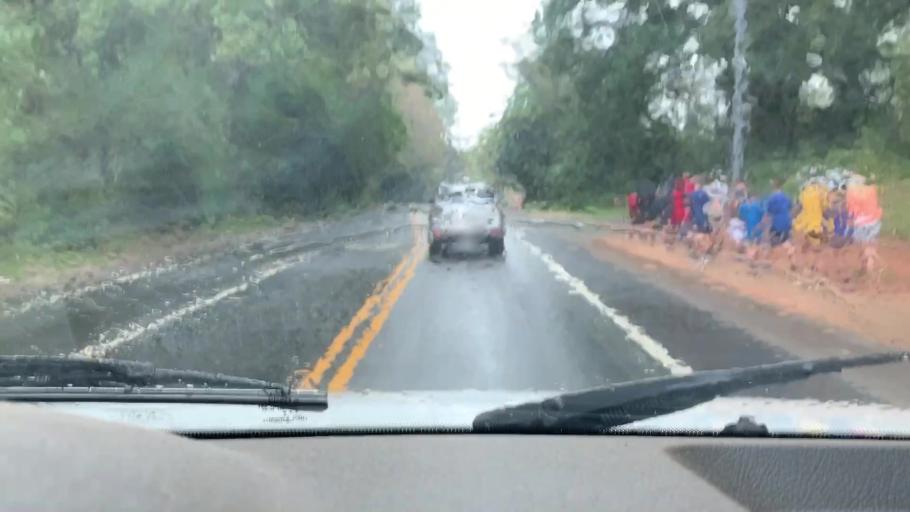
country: US
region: North Carolina
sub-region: Mecklenburg County
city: Cornelius
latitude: 35.5026
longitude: -80.8582
